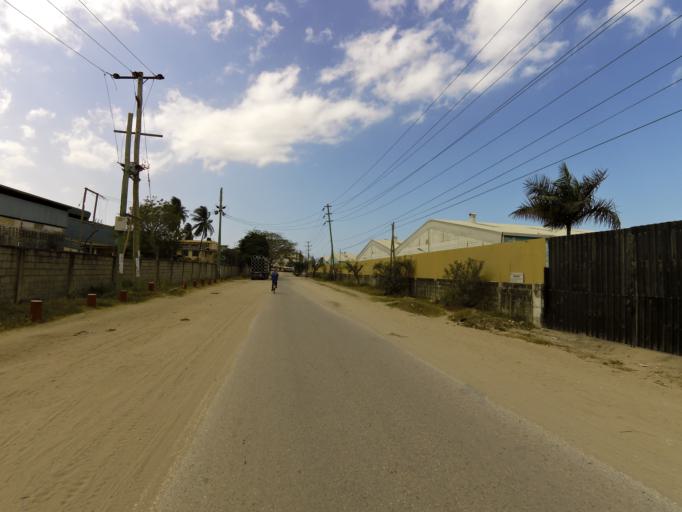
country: TZ
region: Dar es Salaam
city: Magomeni
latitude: -6.7976
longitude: 39.2183
